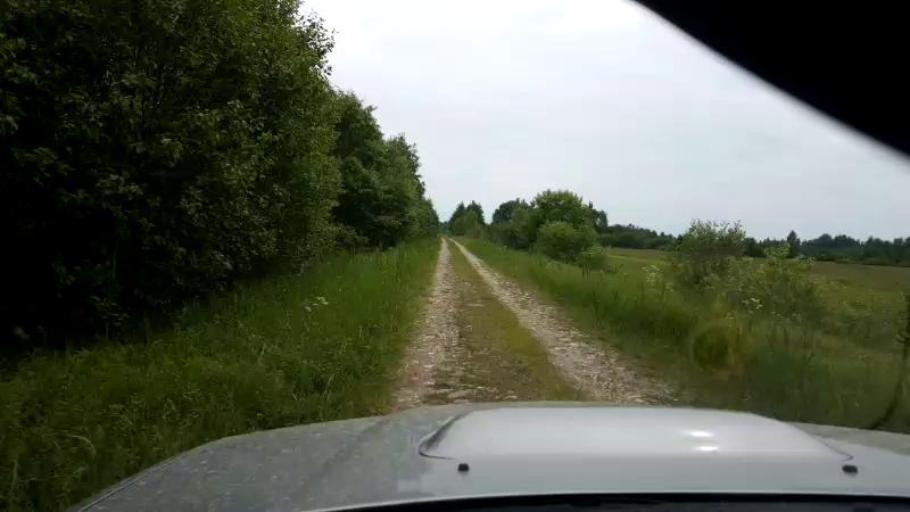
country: EE
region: Paernumaa
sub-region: Tootsi vald
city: Tootsi
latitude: 58.5618
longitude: 24.6886
